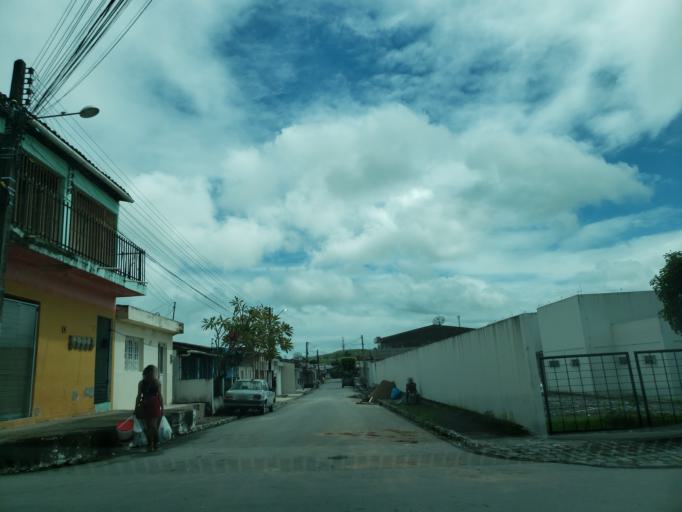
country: BR
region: Alagoas
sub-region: Uniao Dos Palmares
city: Uniao dos Palmares
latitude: -9.1583
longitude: -36.0258
